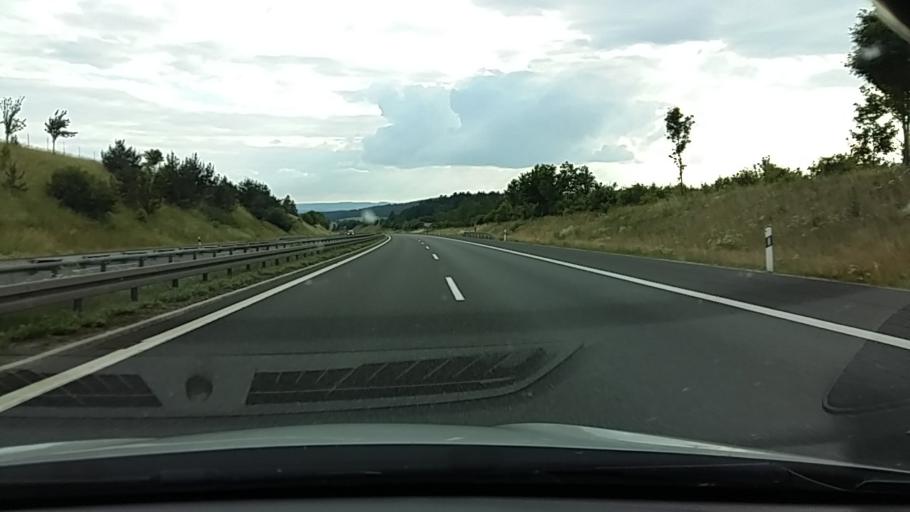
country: DE
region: Bavaria
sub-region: Upper Palatinate
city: Leuchtenberg
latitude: 49.5674
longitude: 12.2163
